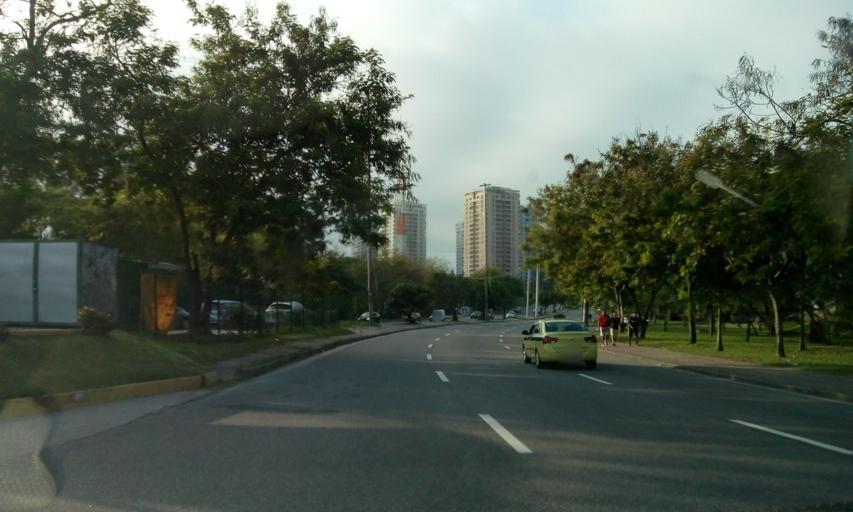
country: BR
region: Rio de Janeiro
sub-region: Rio De Janeiro
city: Rio de Janeiro
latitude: -23.0035
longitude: -43.3664
